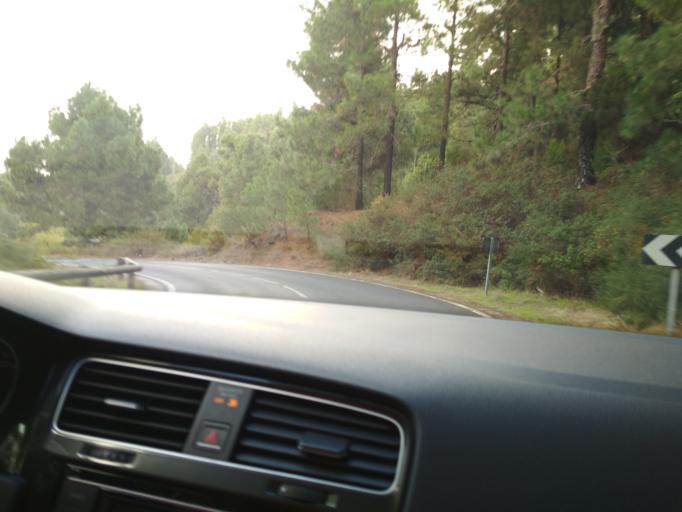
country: ES
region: Canary Islands
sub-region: Provincia de Santa Cruz de Tenerife
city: Garachico
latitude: 28.3358
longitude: -16.7581
